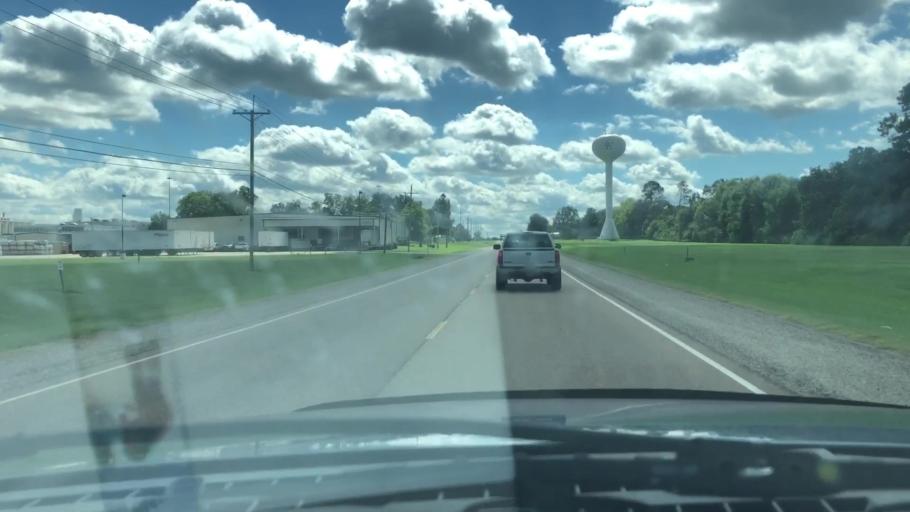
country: US
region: Texas
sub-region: Bowie County
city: Wake Village
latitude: 33.3811
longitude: -94.0921
